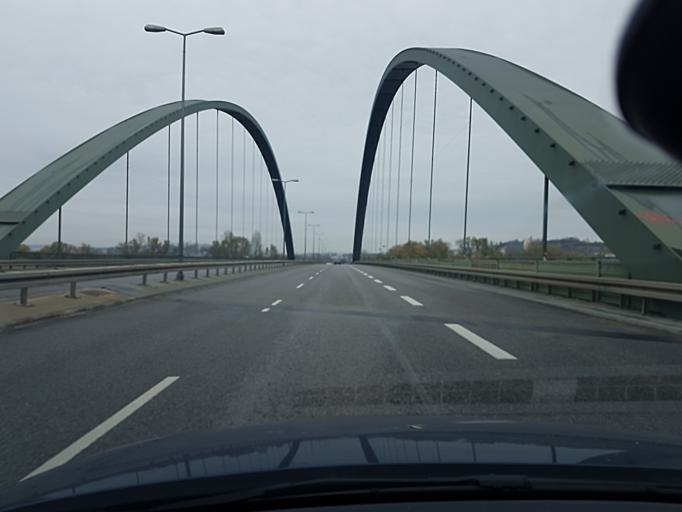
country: DE
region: Bavaria
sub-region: Upper Palatinate
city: Regensburg
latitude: 49.0218
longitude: 12.1418
